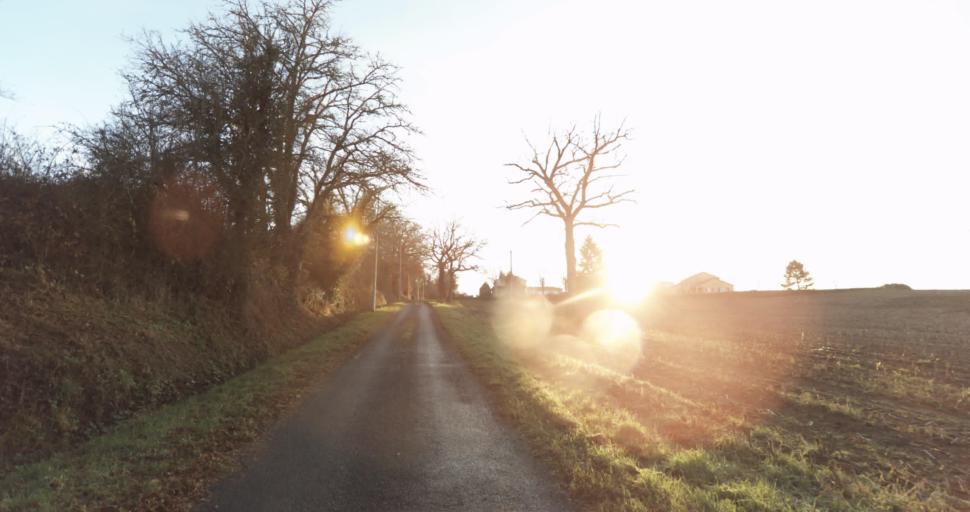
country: FR
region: Limousin
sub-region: Departement de la Haute-Vienne
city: Aixe-sur-Vienne
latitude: 45.7891
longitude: 1.1428
